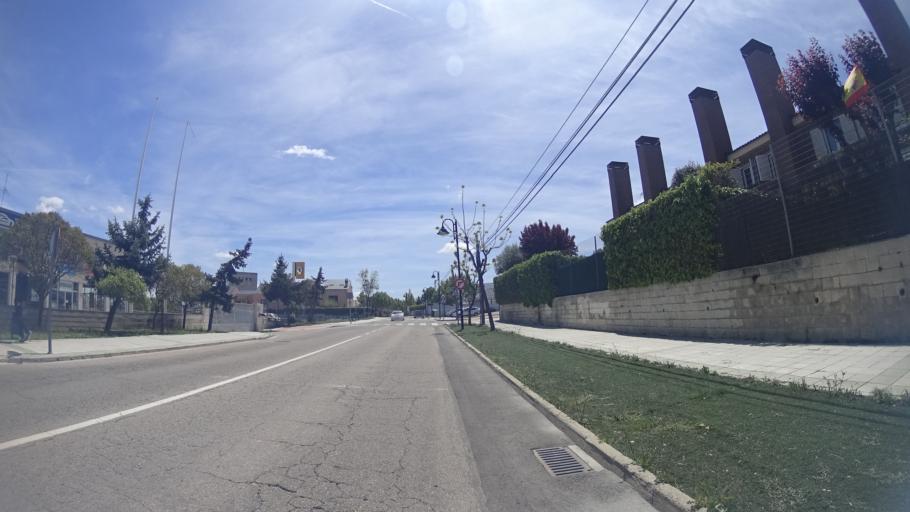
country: ES
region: Madrid
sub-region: Provincia de Madrid
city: Galapagar
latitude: 40.5837
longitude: -4.0102
